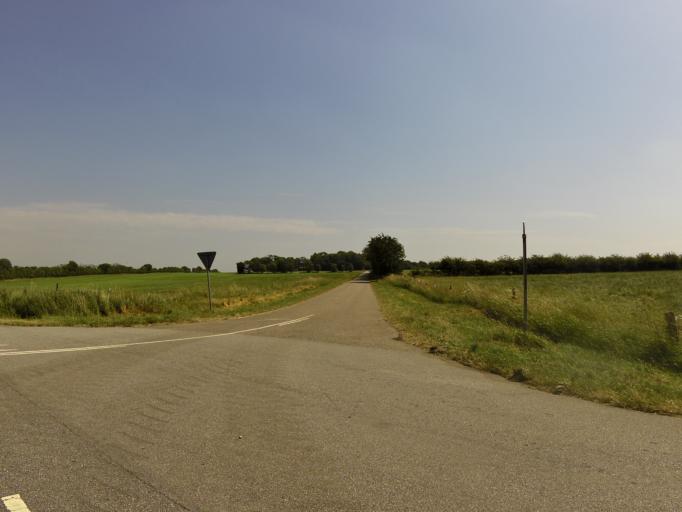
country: DK
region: South Denmark
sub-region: Haderslev Kommune
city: Vojens
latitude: 55.1573
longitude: 9.2610
